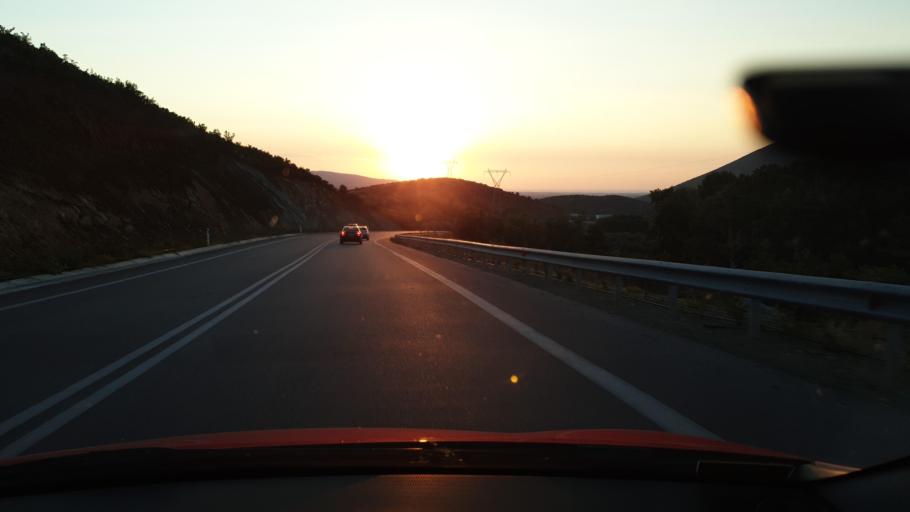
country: GR
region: Central Macedonia
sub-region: Nomos Chalkidikis
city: Galatista
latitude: 40.4640
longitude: 23.2181
